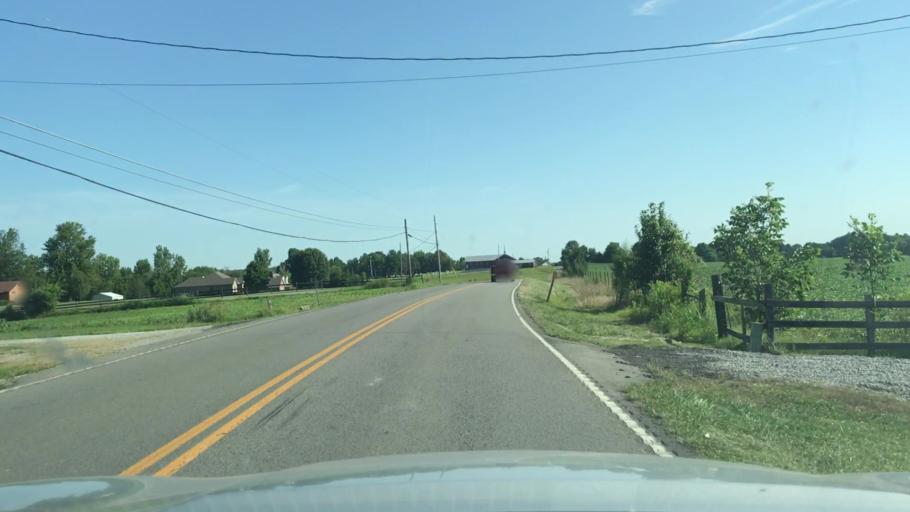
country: US
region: Kentucky
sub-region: Muhlenberg County
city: Greenville
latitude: 37.1758
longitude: -87.1528
